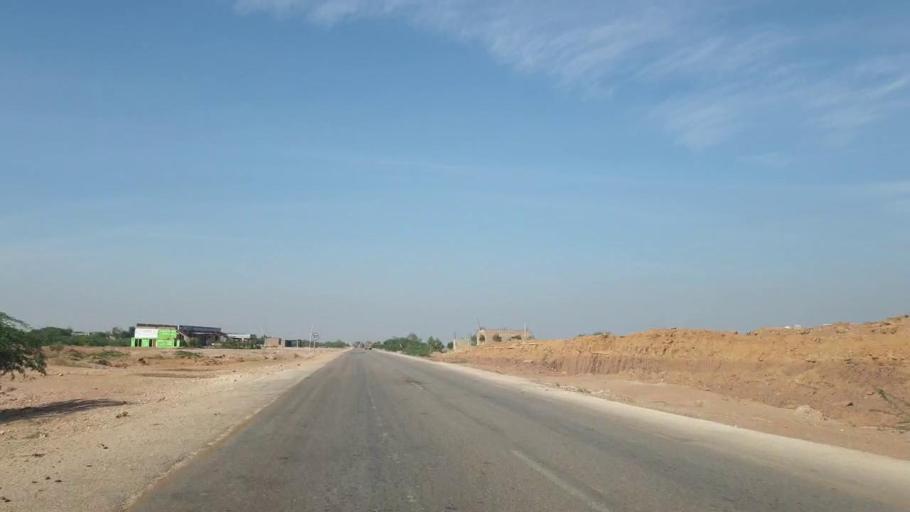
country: PK
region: Sindh
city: Sehwan
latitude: 26.3754
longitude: 67.8733
